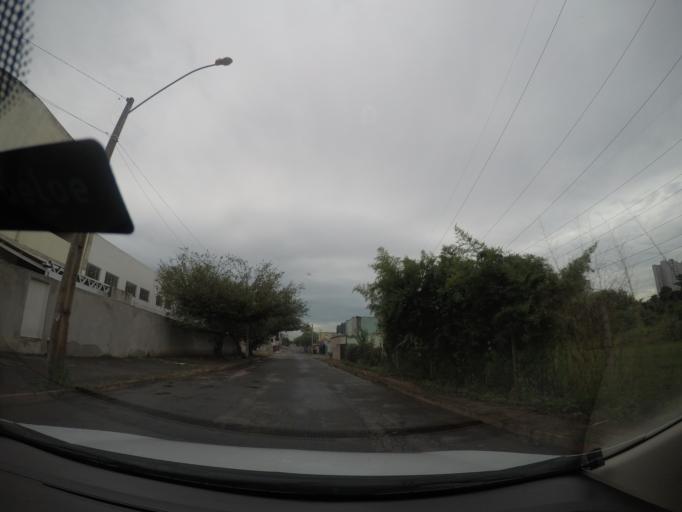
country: BR
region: Goias
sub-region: Goiania
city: Goiania
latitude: -16.6503
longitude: -49.2627
